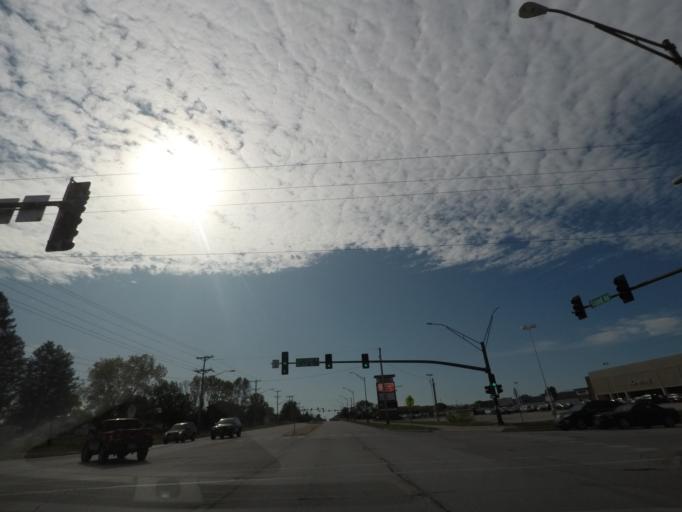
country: US
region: Iowa
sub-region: Story County
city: Ames
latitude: 42.0508
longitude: -93.6205
